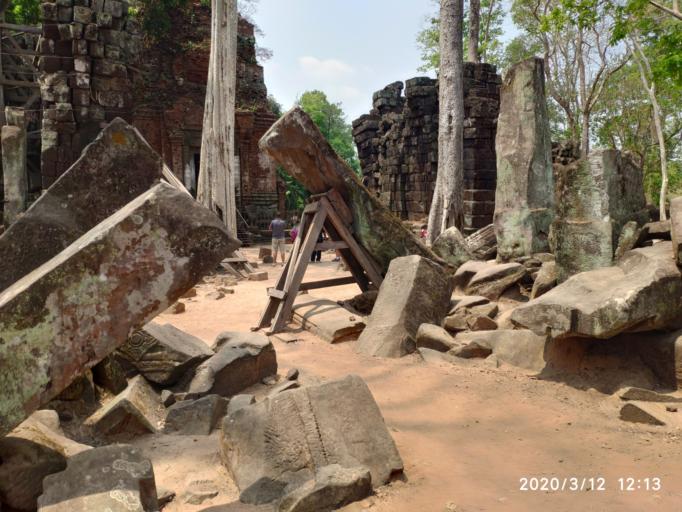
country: KH
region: Preah Vihear
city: Tbeng Meanchey
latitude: 13.7838
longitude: 104.5402
